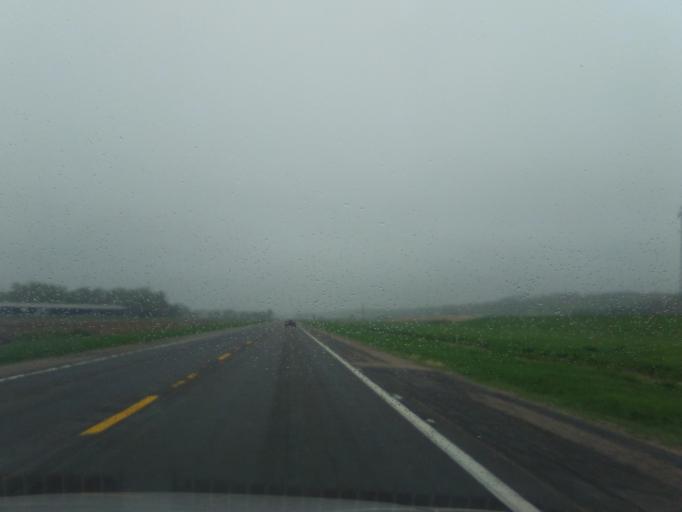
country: US
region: Nebraska
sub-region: Cuming County
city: Wisner
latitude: 41.9685
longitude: -96.8876
